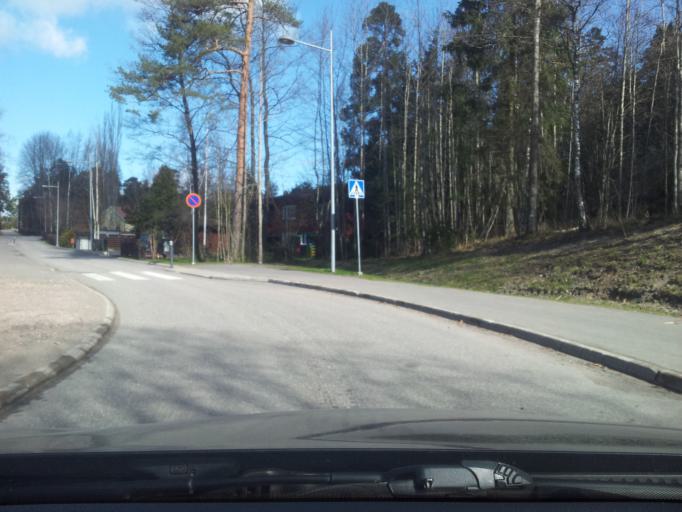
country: FI
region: Uusimaa
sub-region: Helsinki
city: Kauniainen
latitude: 60.1692
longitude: 24.7090
